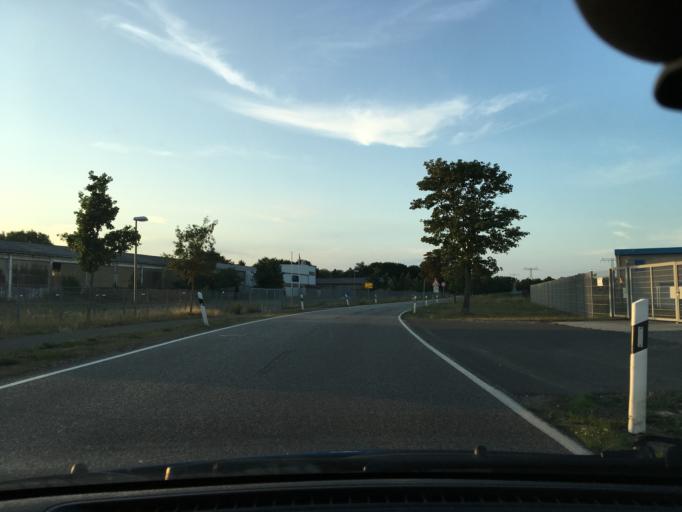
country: DE
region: Mecklenburg-Vorpommern
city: Boizenburg
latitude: 53.3826
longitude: 10.7494
